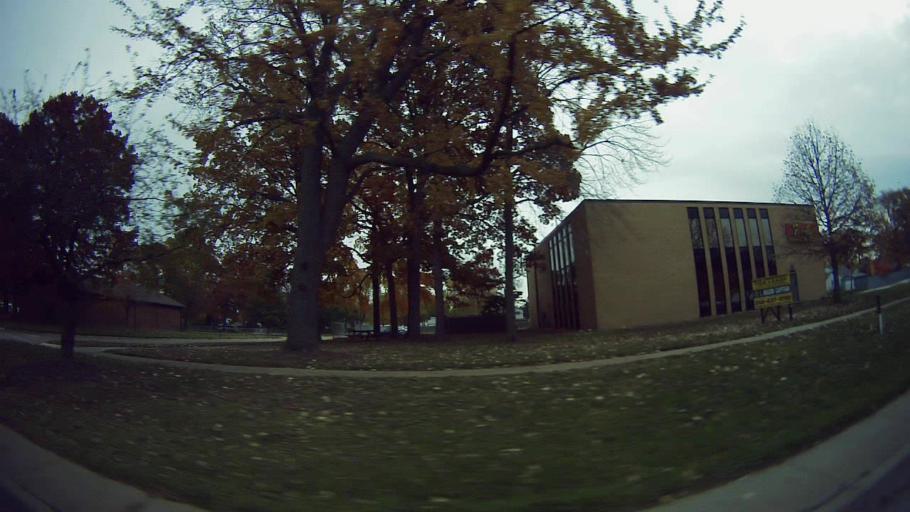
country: US
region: Michigan
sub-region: Oakland County
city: Madison Heights
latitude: 42.4967
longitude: -83.1055
